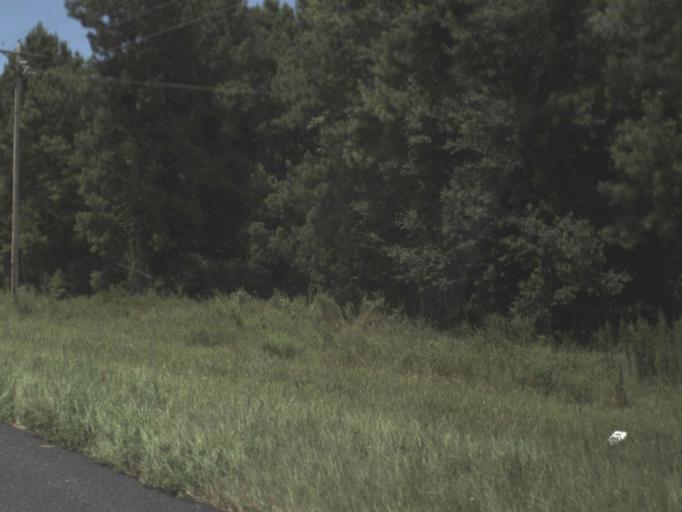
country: US
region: Florida
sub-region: Jefferson County
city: Monticello
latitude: 30.3146
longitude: -83.7583
